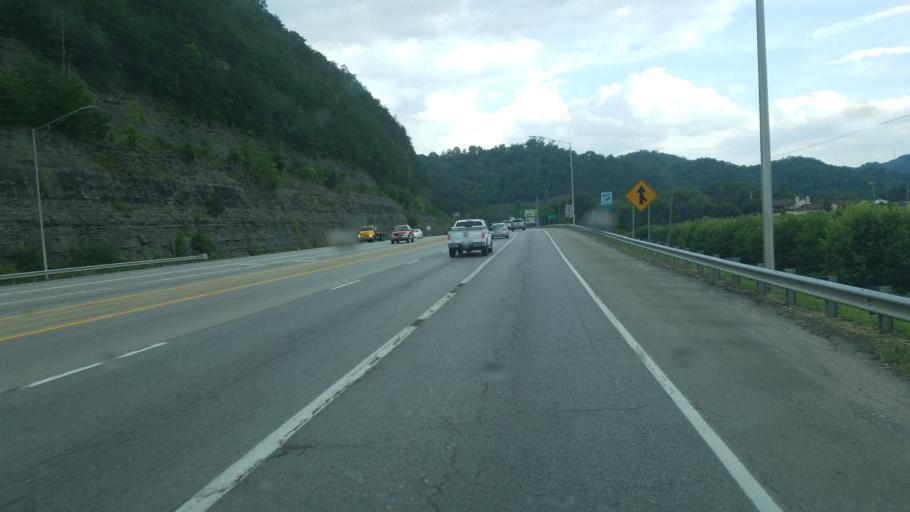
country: US
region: Kentucky
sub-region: Pike County
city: Pikeville
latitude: 37.5030
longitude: -82.5324
